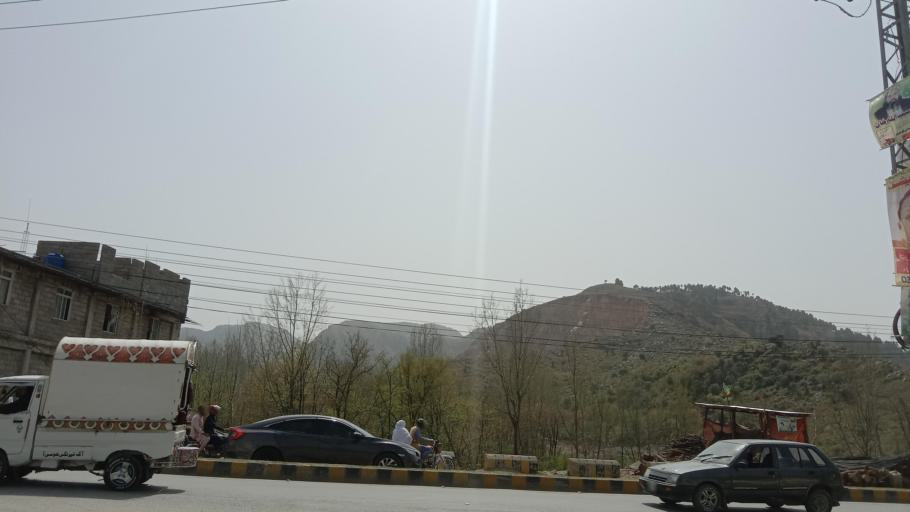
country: PK
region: Khyber Pakhtunkhwa
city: Abbottabad
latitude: 34.1581
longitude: 73.2491
